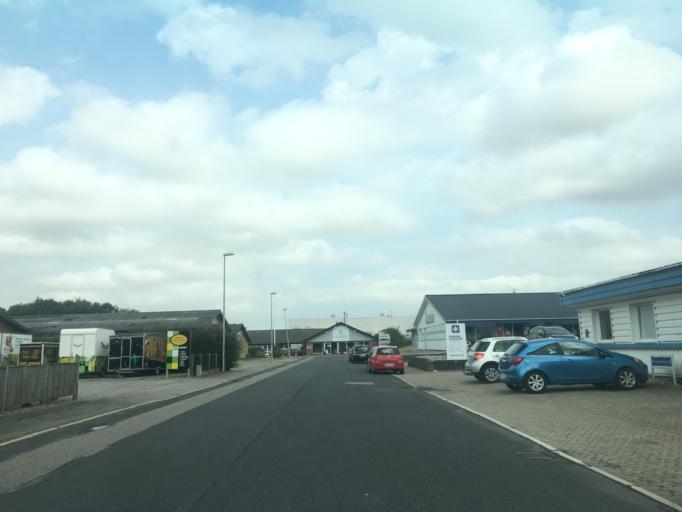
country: DK
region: Central Jutland
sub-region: Holstebro Kommune
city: Holstebro
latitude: 56.3813
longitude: 8.6120
